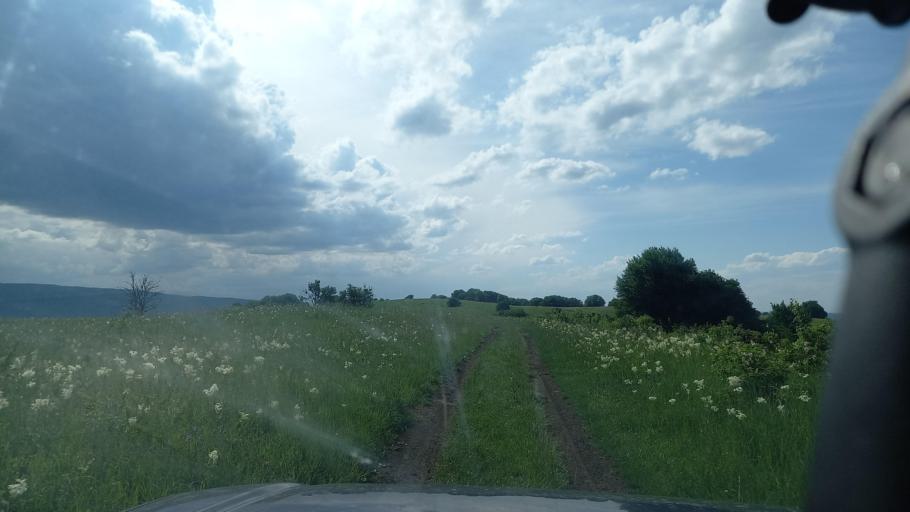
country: RU
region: Karachayevo-Cherkesiya
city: Kurdzhinovo
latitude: 44.1244
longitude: 41.0902
